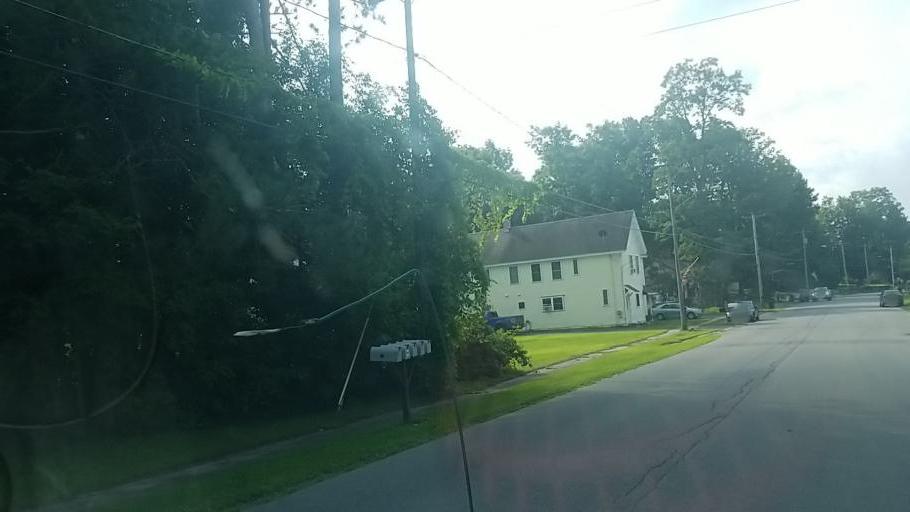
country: US
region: New York
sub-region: Fulton County
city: Broadalbin
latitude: 43.1086
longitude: -74.2631
